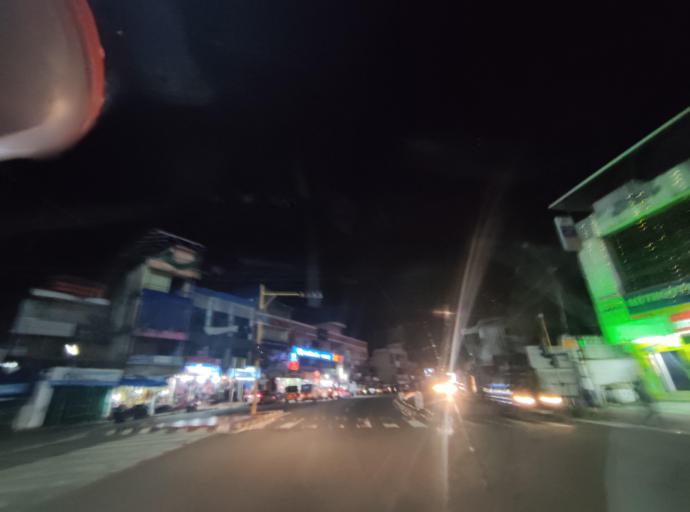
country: IN
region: Kerala
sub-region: Thiruvananthapuram
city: Attingal
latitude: 8.7702
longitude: 76.8810
